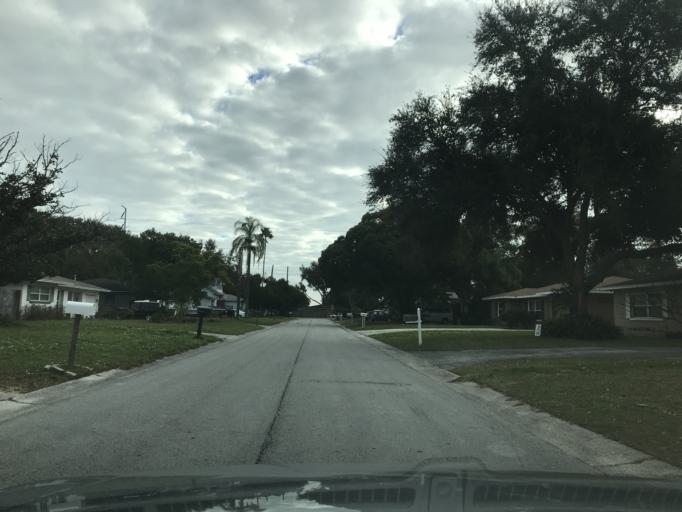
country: US
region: Florida
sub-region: Pinellas County
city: Belleair
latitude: 27.9453
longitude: -82.7766
